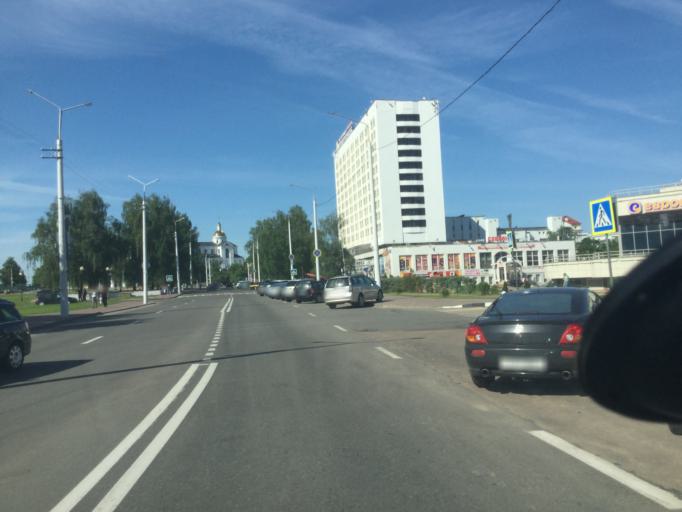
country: BY
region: Vitebsk
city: Vitebsk
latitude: 55.1905
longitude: 30.2015
